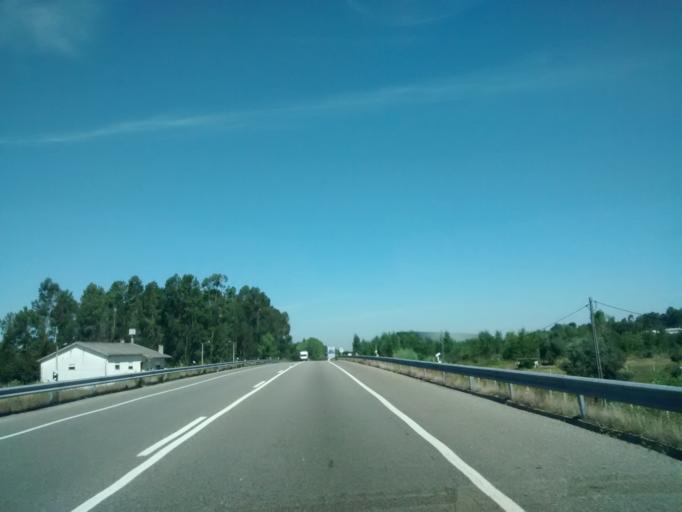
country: PT
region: Aveiro
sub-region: Anadia
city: Sangalhos
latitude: 40.4749
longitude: -8.4729
